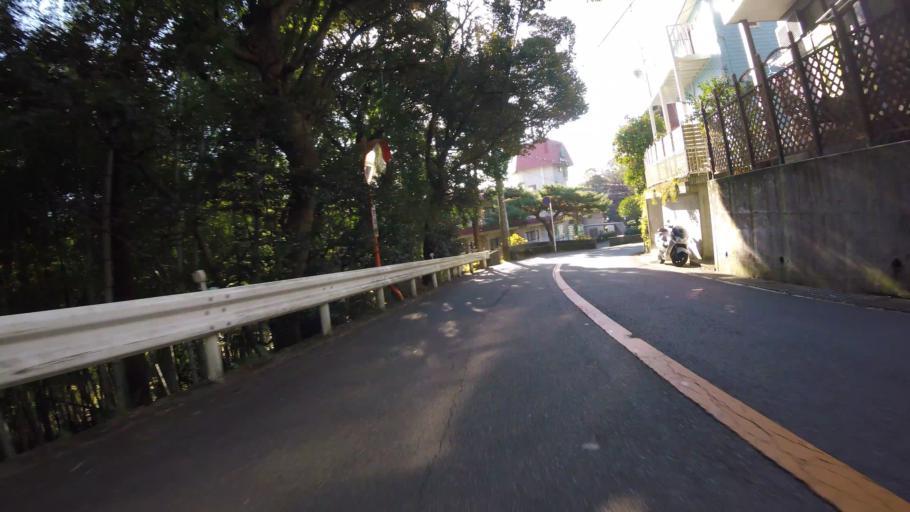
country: JP
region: Shizuoka
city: Atami
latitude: 35.1057
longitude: 139.0634
